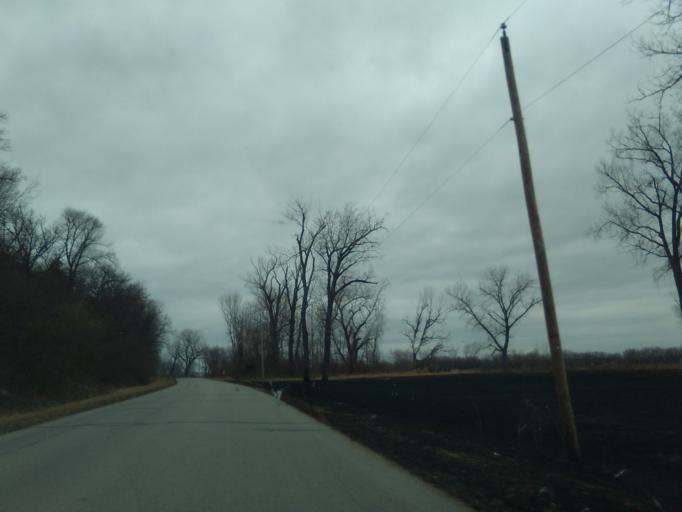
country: US
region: Missouri
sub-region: Holt County
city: Mound City
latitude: 40.0268
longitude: -95.3752
